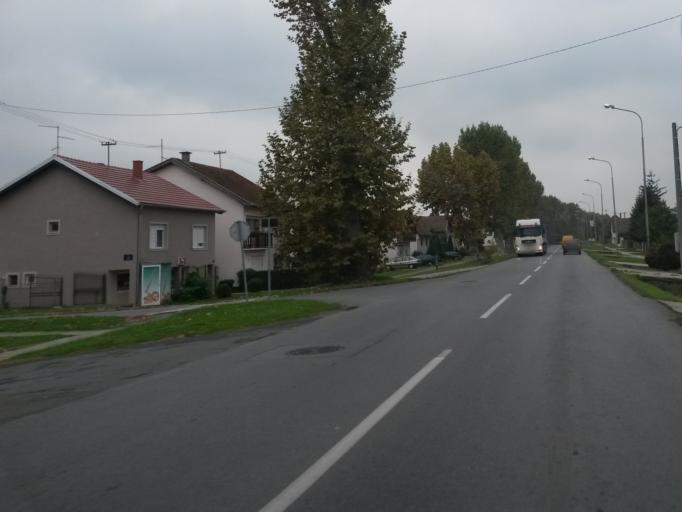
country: HR
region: Osjecko-Baranjska
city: Visnjevac
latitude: 45.5342
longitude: 18.6317
